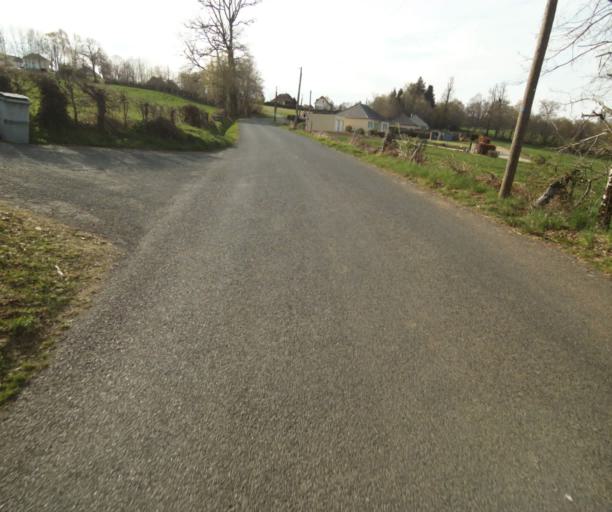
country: FR
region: Limousin
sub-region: Departement de la Correze
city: Naves
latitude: 45.2940
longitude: 1.7454
